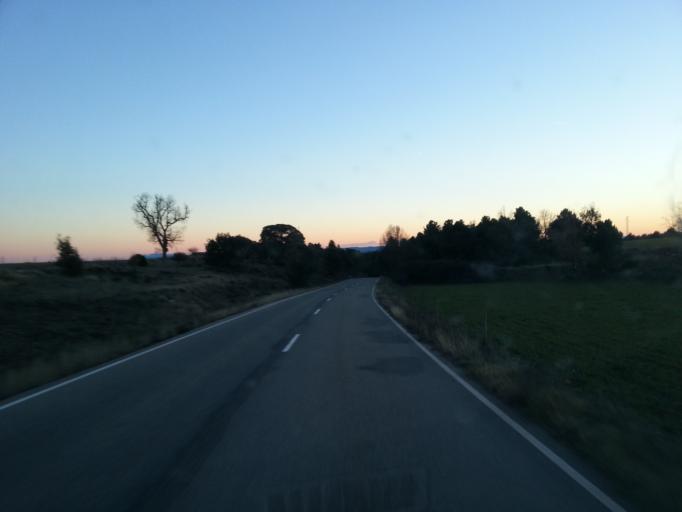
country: ES
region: Catalonia
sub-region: Provincia de Lleida
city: Solsona
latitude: 42.0646
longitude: 1.5109
